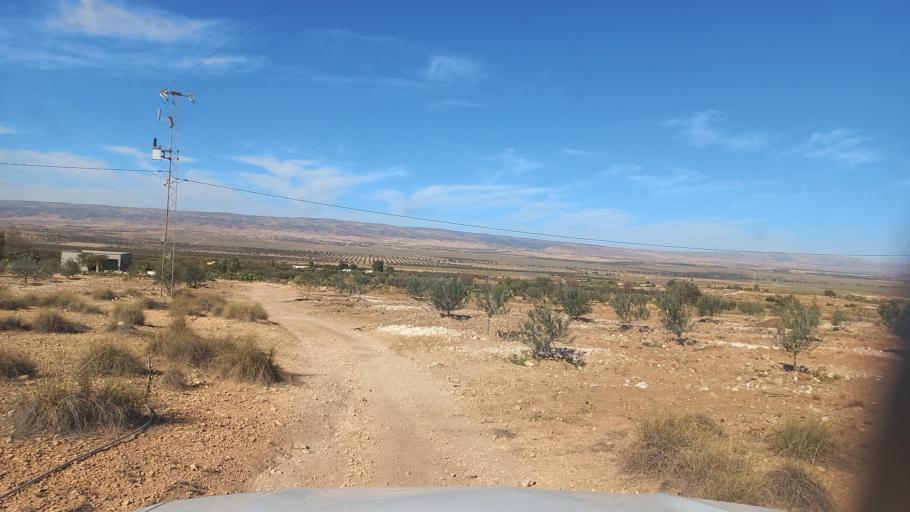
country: TN
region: Al Qasrayn
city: Kasserine
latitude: 35.2007
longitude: 8.9722
